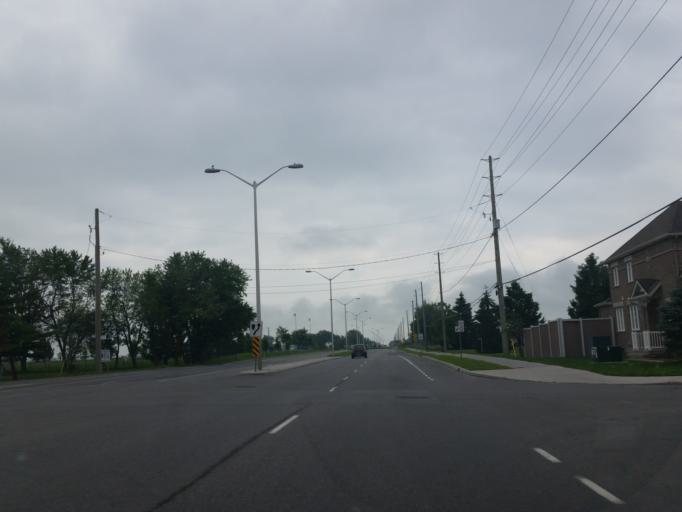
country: CA
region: Ontario
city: Clarence-Rockland
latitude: 45.4684
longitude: -75.4531
